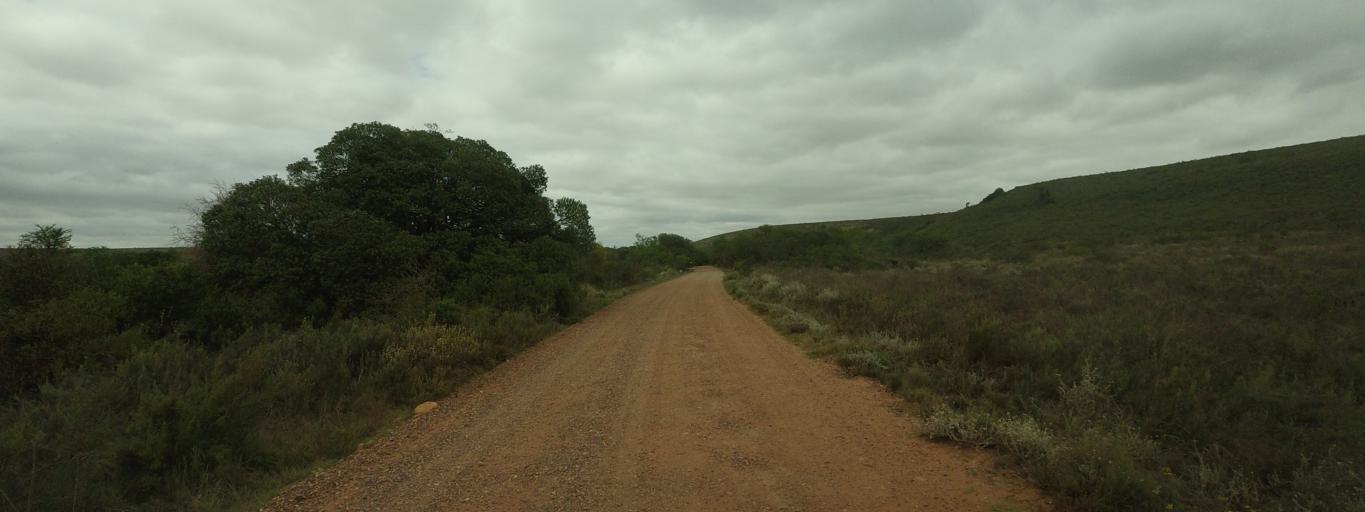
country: ZA
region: Western Cape
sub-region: Overberg District Municipality
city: Swellendam
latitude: -34.0659
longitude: 20.4373
